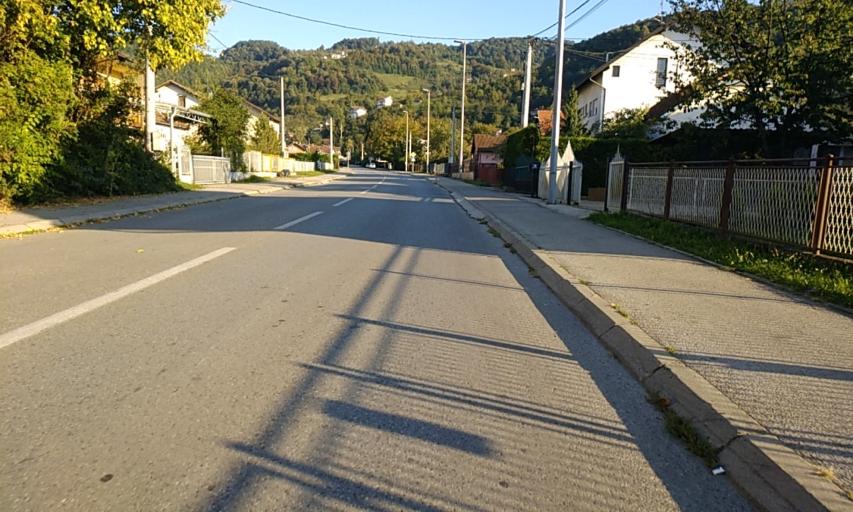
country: BA
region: Republika Srpska
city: Mejdan - Obilicevo
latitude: 44.7581
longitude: 17.1861
